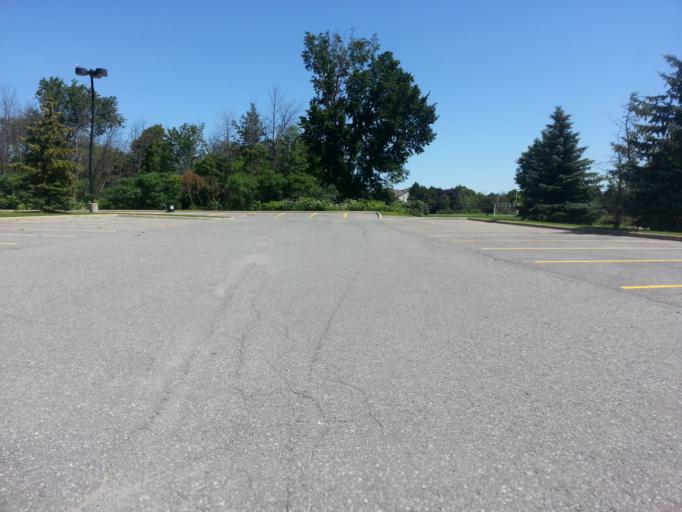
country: CA
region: Ontario
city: Bells Corners
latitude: 45.3229
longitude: -75.9239
